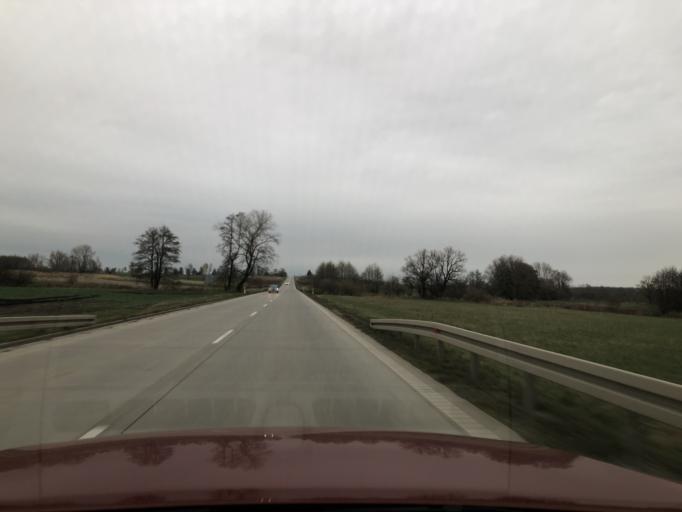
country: PL
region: Lower Silesian Voivodeship
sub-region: Powiat swidnicki
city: Swidnica
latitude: 50.8661
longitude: 16.4677
